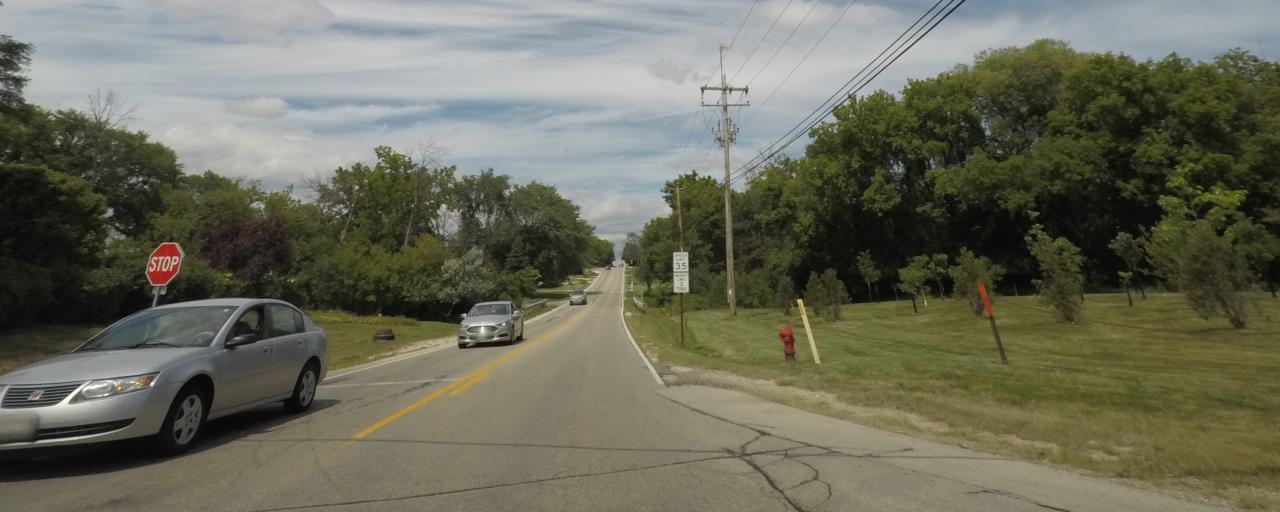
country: US
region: Wisconsin
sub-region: Waukesha County
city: New Berlin
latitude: 42.9737
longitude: -88.0689
